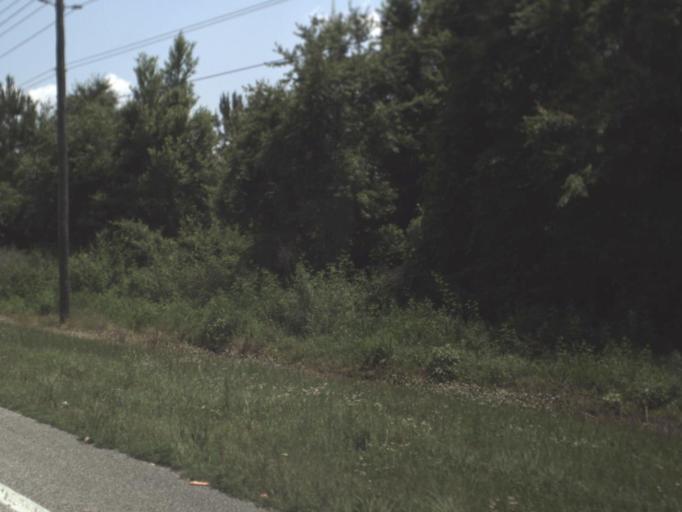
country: US
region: Florida
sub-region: Duval County
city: Baldwin
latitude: 30.2616
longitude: -81.9915
